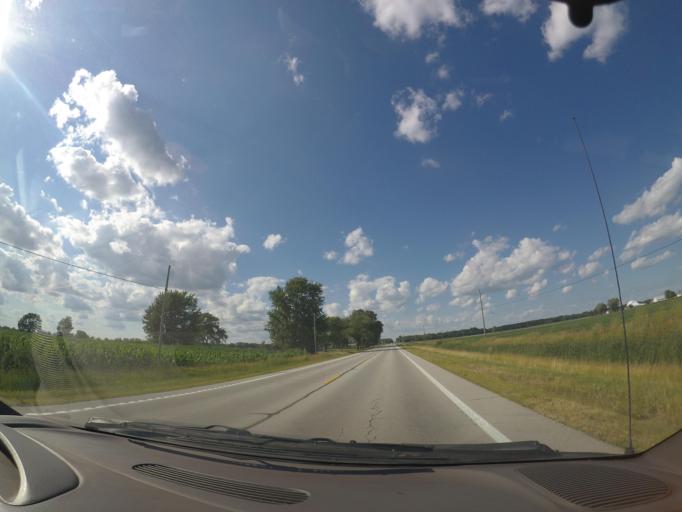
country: US
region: Ohio
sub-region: Sandusky County
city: Woodville
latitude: 41.4656
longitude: -83.4150
